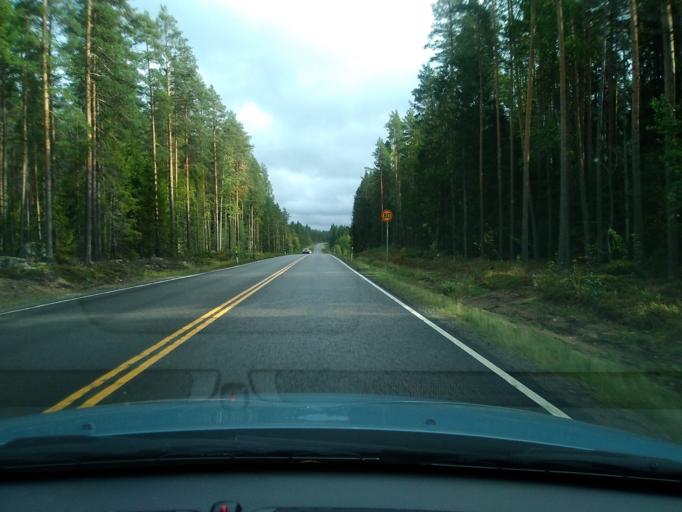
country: FI
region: Central Finland
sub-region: Saarijaervi-Viitasaari
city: Saarijaervi
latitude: 62.6772
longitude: 25.3855
